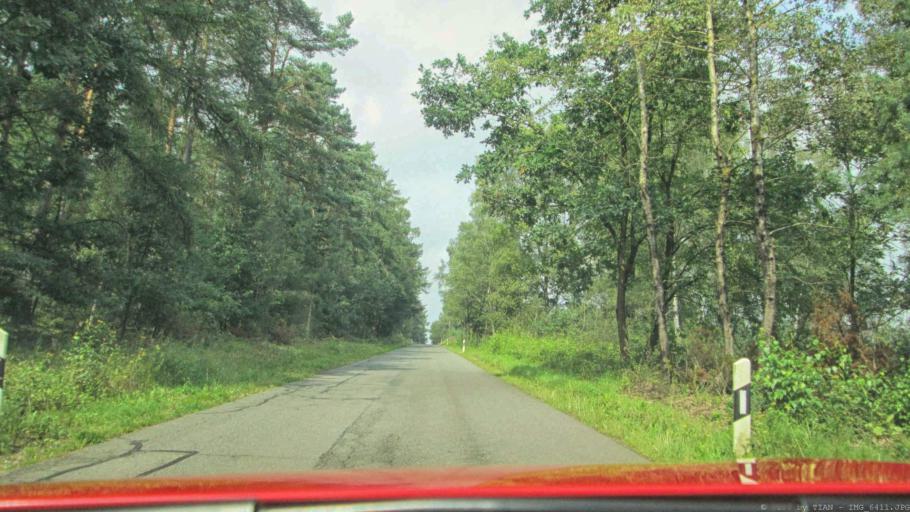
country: DE
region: Lower Saxony
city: Obernholz
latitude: 52.7905
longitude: 10.5639
